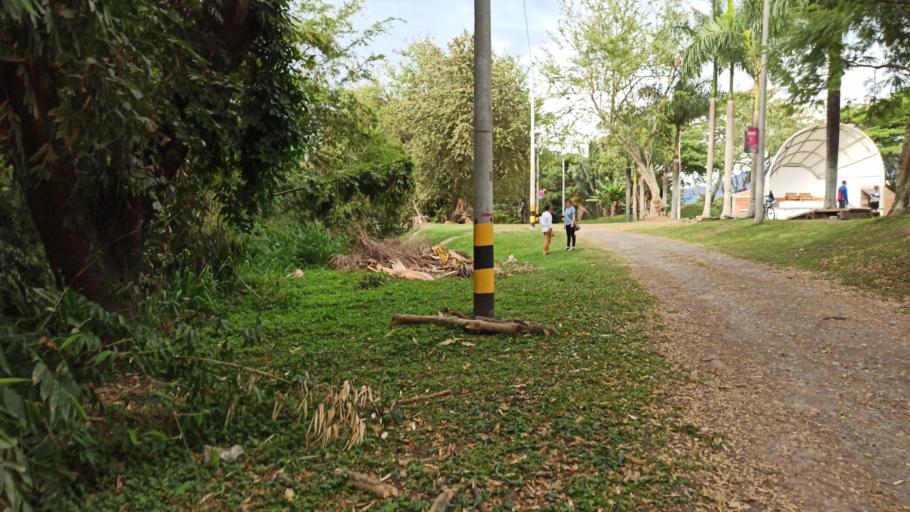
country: CO
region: Valle del Cauca
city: Palmira
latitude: 3.5305
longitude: -76.2845
